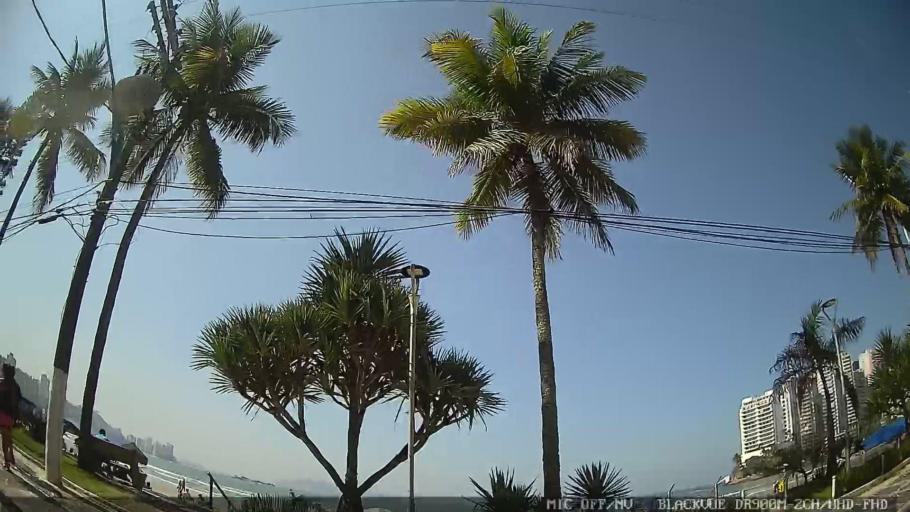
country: BR
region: Sao Paulo
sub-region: Guaruja
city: Guaruja
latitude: -24.0081
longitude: -46.2690
